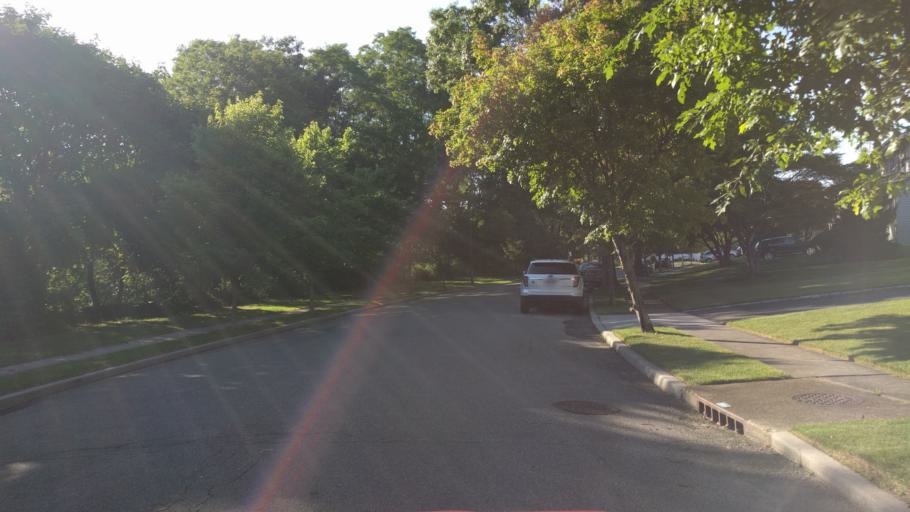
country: US
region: New York
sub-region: Nassau County
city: East Norwich
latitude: 40.8517
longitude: -73.5332
